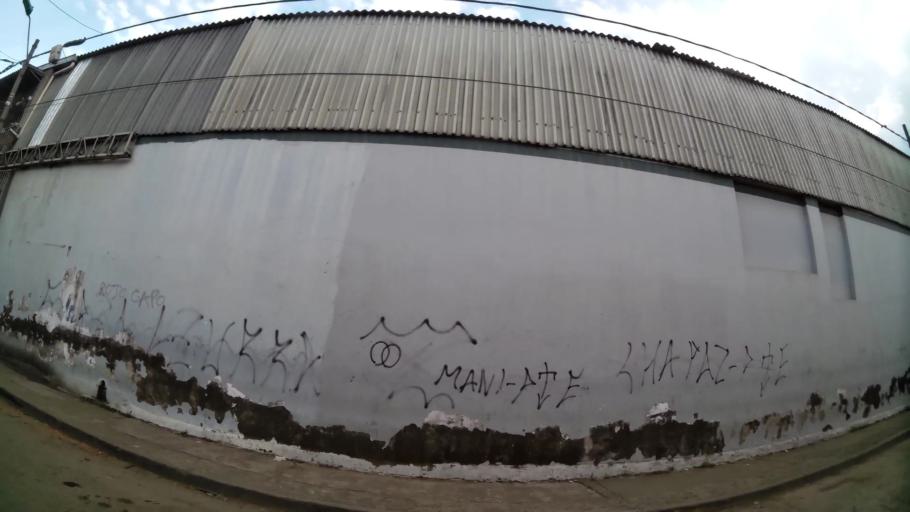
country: CO
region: Valle del Cauca
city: Cali
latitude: 3.4585
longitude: -76.5126
